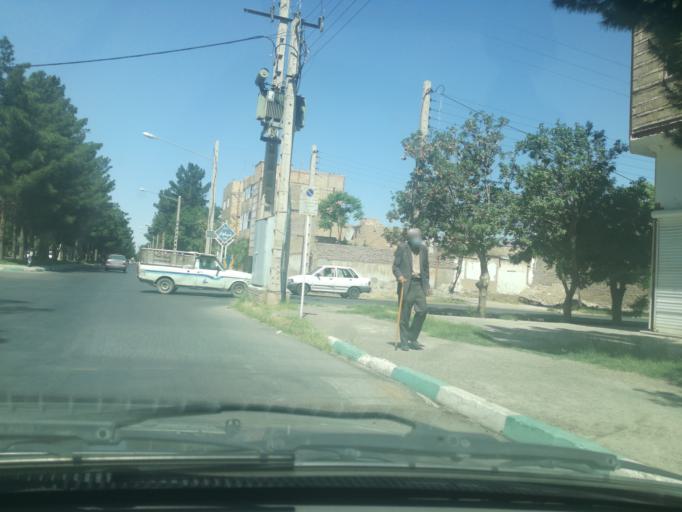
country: IR
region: Razavi Khorasan
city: Sarakhs
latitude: 36.5378
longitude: 61.1531
